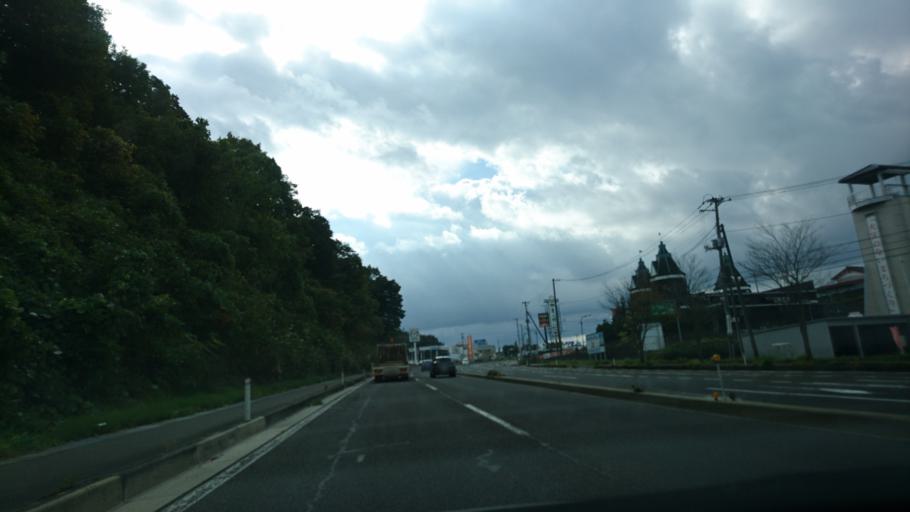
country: JP
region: Miyagi
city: Tomiya
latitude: 38.3623
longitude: 140.8735
